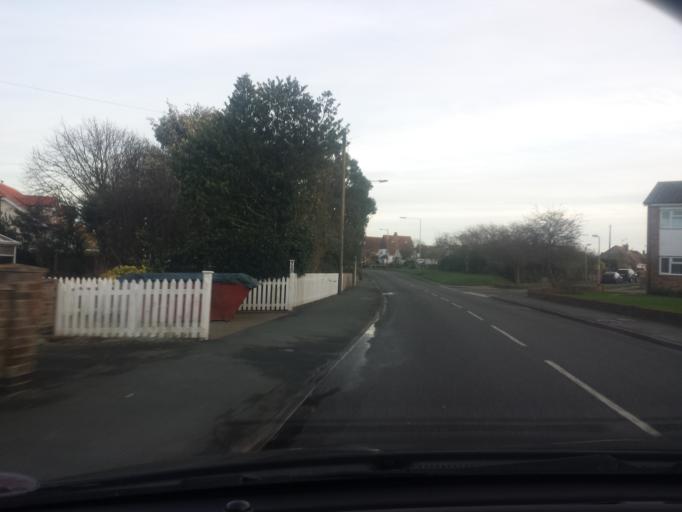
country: GB
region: England
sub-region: Essex
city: Clacton-on-Sea
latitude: 51.8052
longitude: 1.1997
